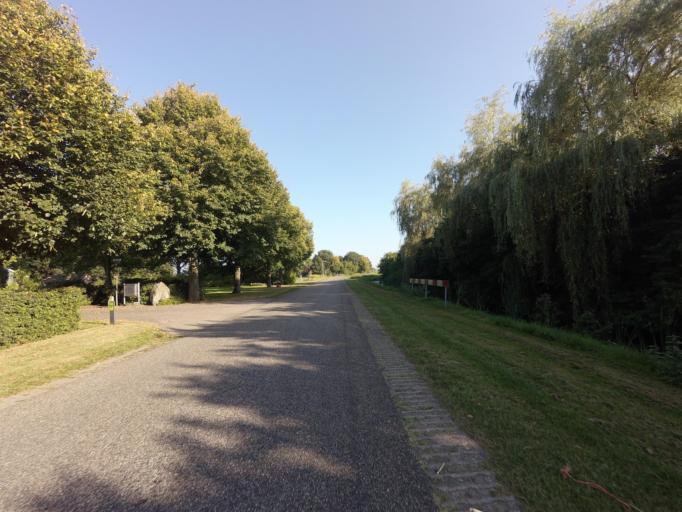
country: NL
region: Overijssel
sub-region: Gemeente Hardenberg
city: Hardenberg
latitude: 52.5534
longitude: 6.6512
